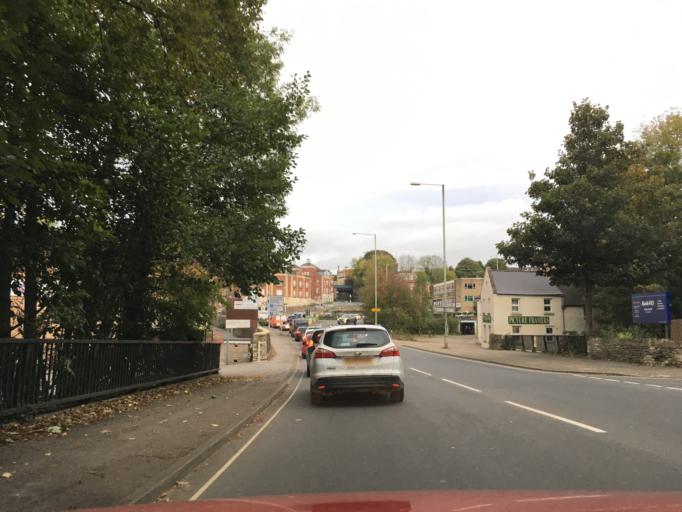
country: GB
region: England
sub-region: Gloucestershire
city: Stroud
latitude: 51.7437
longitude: -2.2235
